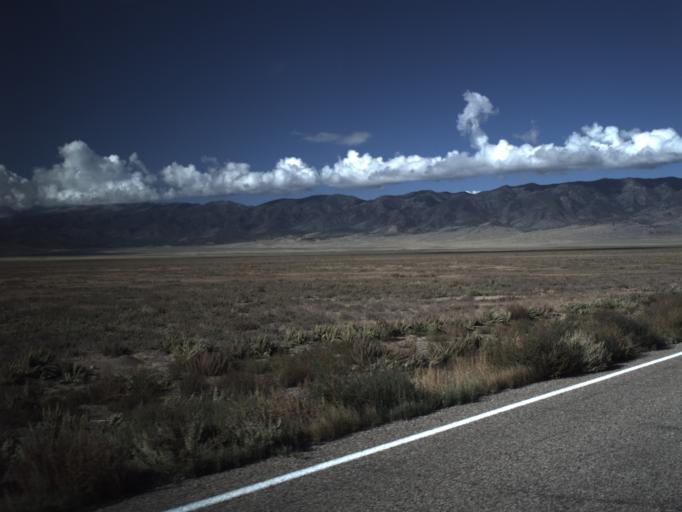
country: US
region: Utah
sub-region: Beaver County
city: Milford
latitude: 38.4585
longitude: -113.3701
